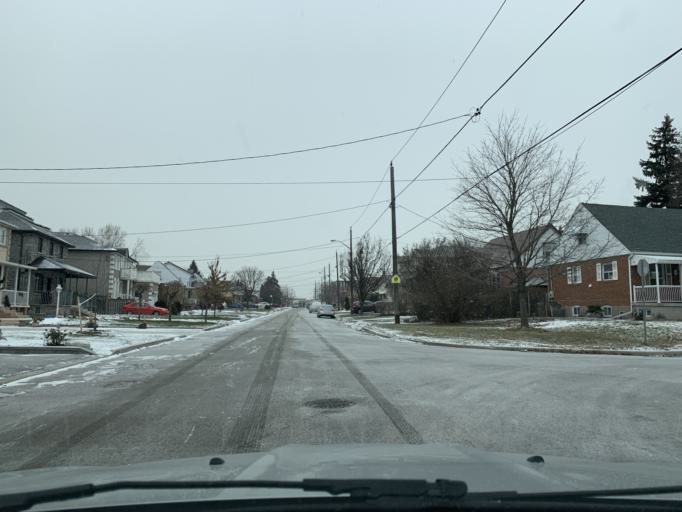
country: CA
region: Ontario
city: Toronto
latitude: 43.7251
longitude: -79.4778
